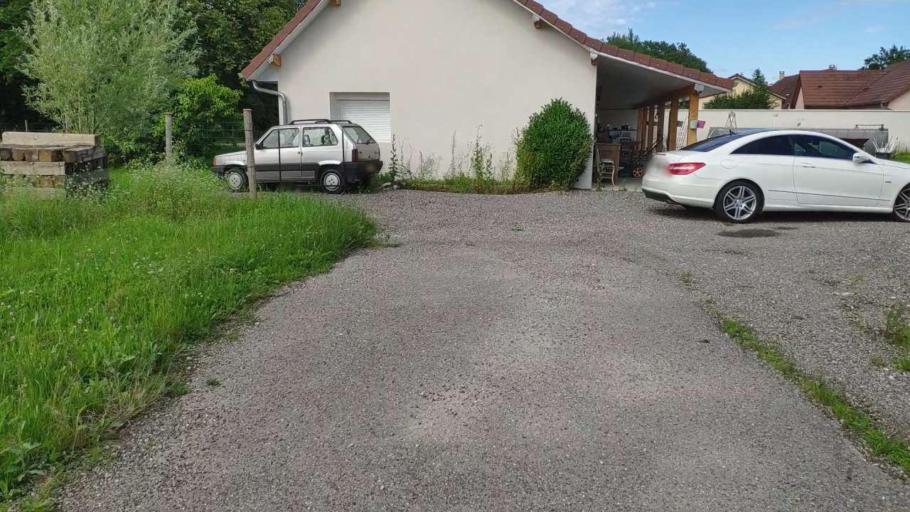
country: FR
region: Franche-Comte
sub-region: Departement du Jura
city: Bletterans
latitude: 46.8055
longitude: 5.4582
